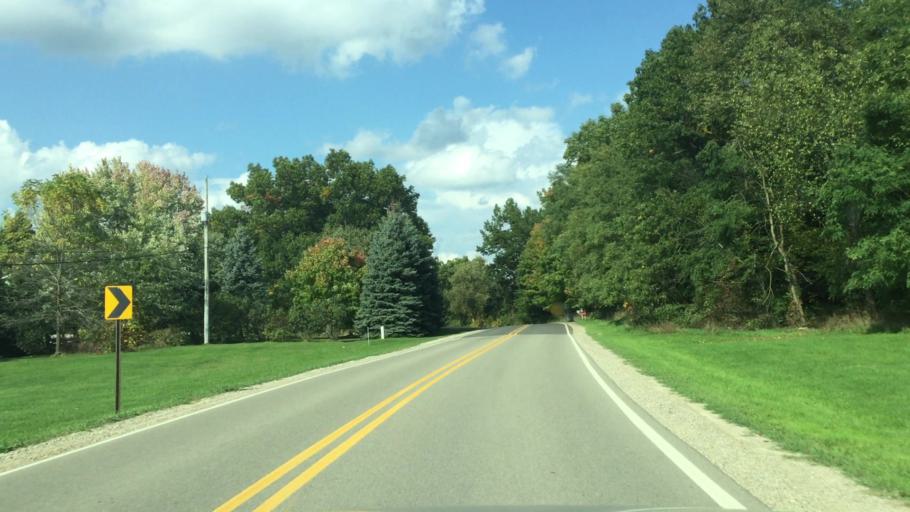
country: US
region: Michigan
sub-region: Genesee County
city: Fenton
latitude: 42.6953
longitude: -83.7031
